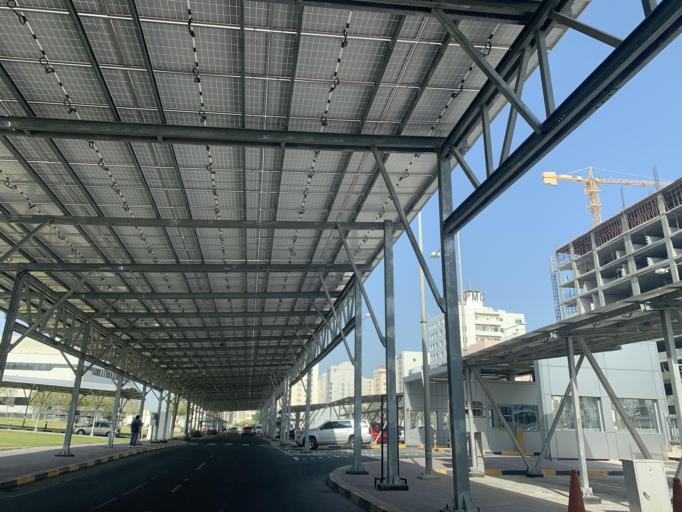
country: BH
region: Muharraq
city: Al Muharraq
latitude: 26.2635
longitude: 50.6011
